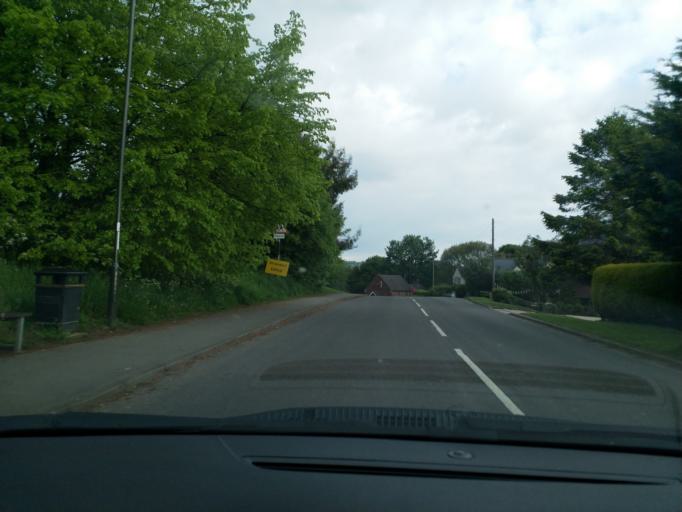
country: GB
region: England
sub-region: Derbyshire
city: Dronfield
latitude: 53.2735
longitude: -1.4905
